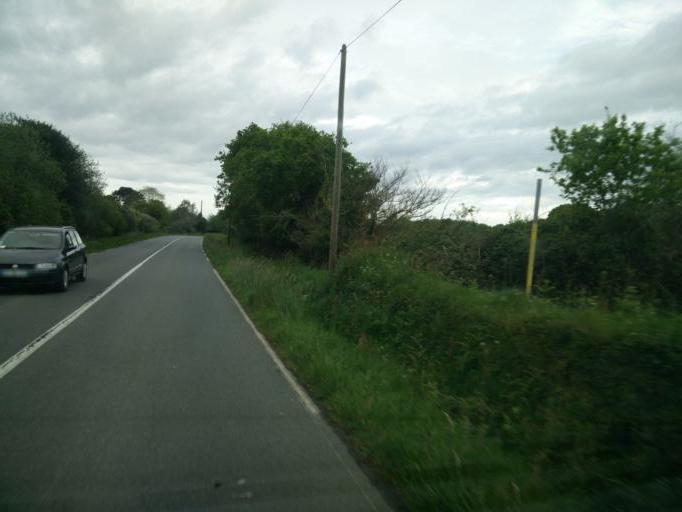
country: FR
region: Brittany
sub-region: Departement des Cotes-d'Armor
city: Ploumilliau
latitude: 48.6949
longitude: -3.5457
